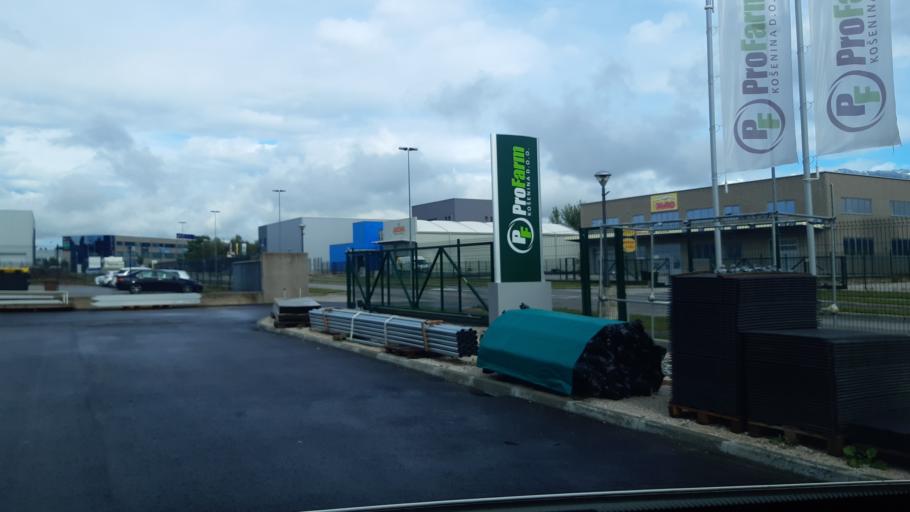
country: SI
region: Komenda
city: Komenda
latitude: 46.1880
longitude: 14.5228
